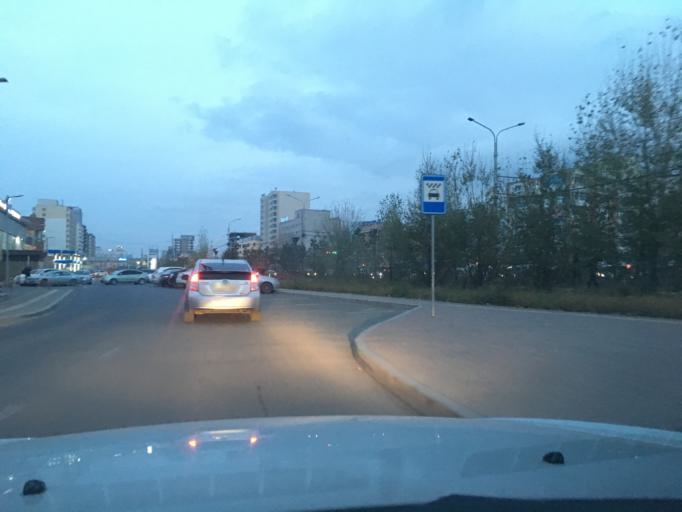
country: MN
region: Ulaanbaatar
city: Ulaanbaatar
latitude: 47.9143
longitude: 106.8694
